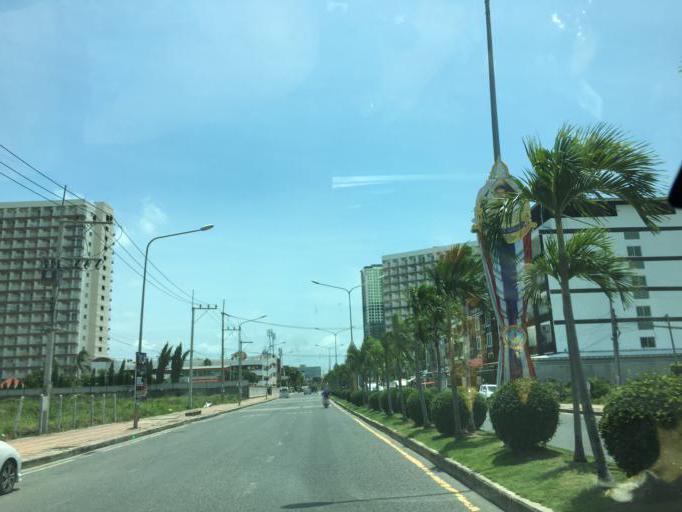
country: TH
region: Chon Buri
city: Phatthaya
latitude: 12.8890
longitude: 100.8806
